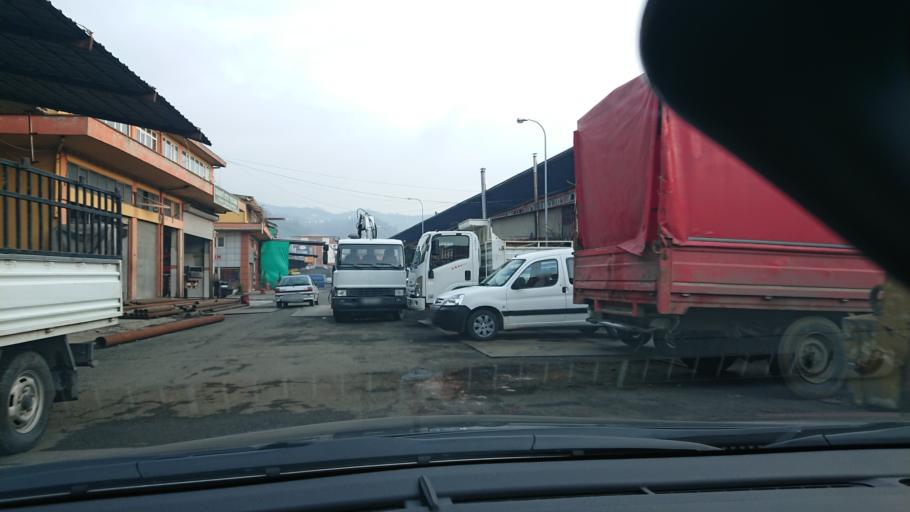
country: TR
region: Rize
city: Gundogdu
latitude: 41.0439
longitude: 40.5754
